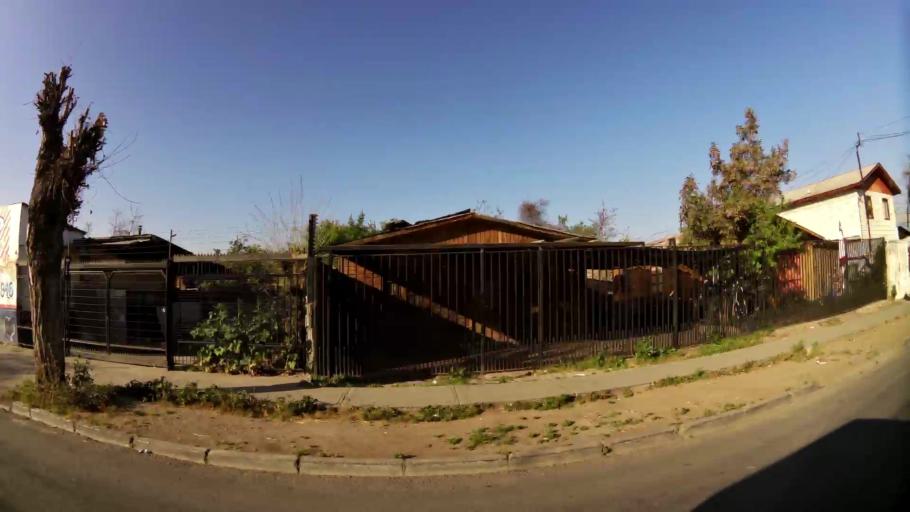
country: CL
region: Santiago Metropolitan
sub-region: Provincia de Santiago
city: Santiago
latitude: -33.3743
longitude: -70.6419
